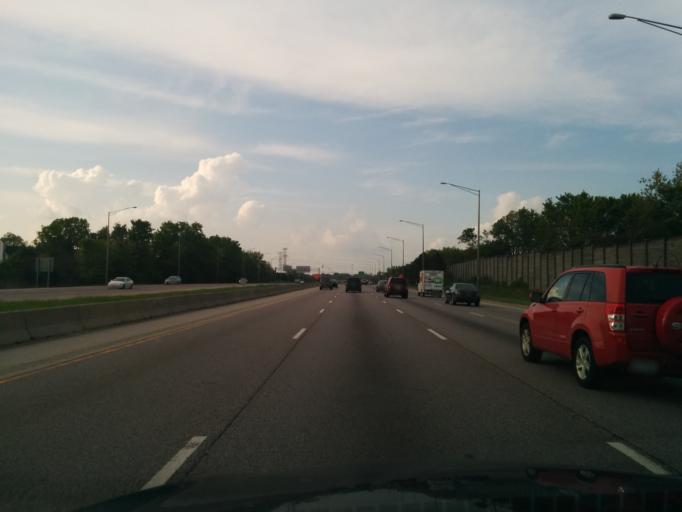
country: US
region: Illinois
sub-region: DuPage County
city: Glendale Heights
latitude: 41.9378
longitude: -88.0375
